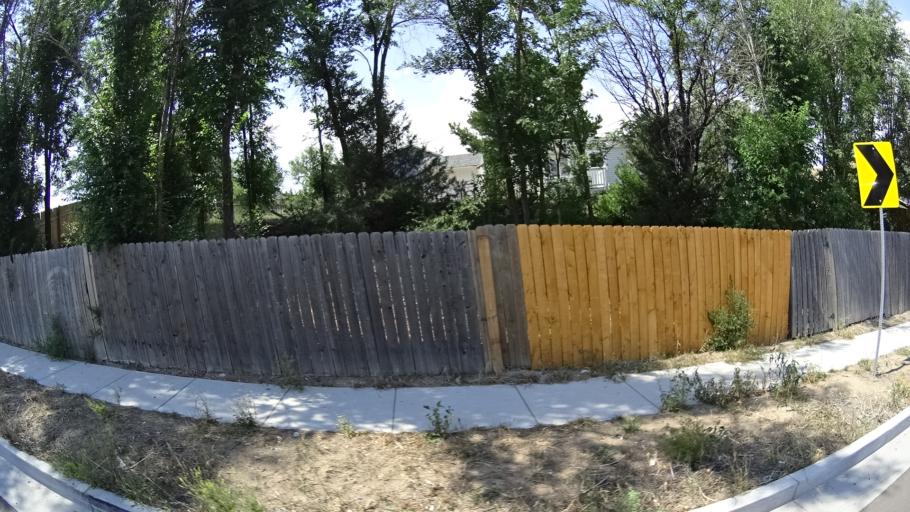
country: US
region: Colorado
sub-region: El Paso County
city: Colorado Springs
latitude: 38.9260
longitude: -104.7856
